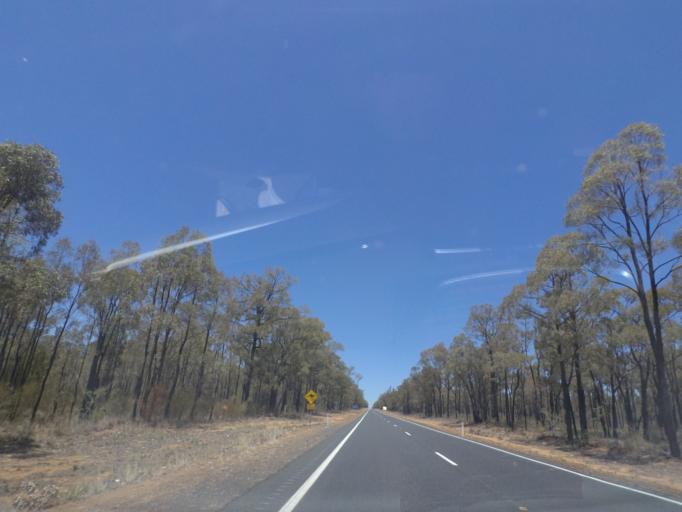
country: AU
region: New South Wales
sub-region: Narrabri
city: Narrabri
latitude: -30.7249
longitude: 149.5236
